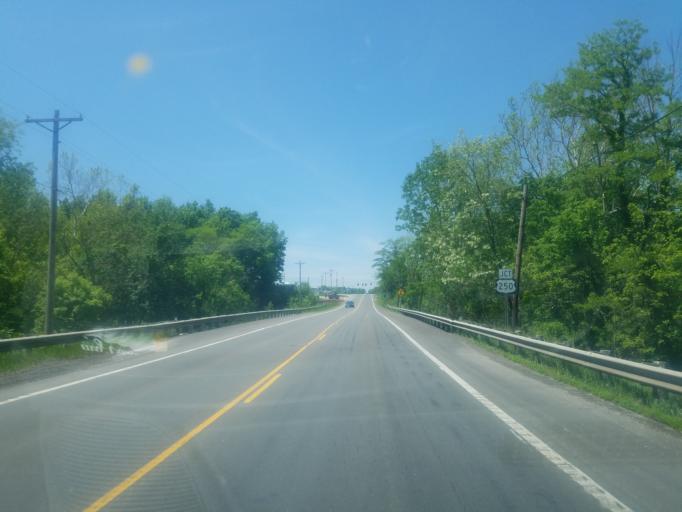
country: US
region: Ohio
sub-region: Huron County
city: New London
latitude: 41.0291
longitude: -82.4142
